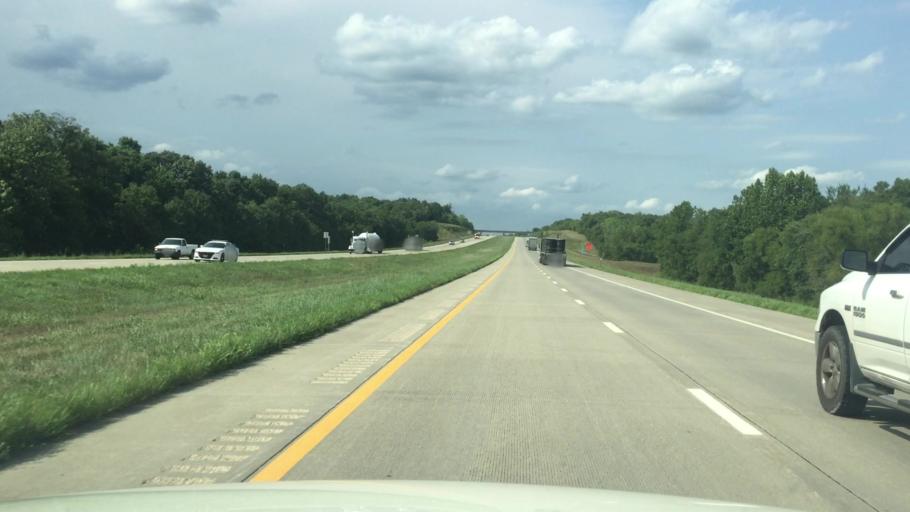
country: US
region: Kansas
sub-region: Miami County
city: Louisburg
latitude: 38.5961
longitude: -94.6940
